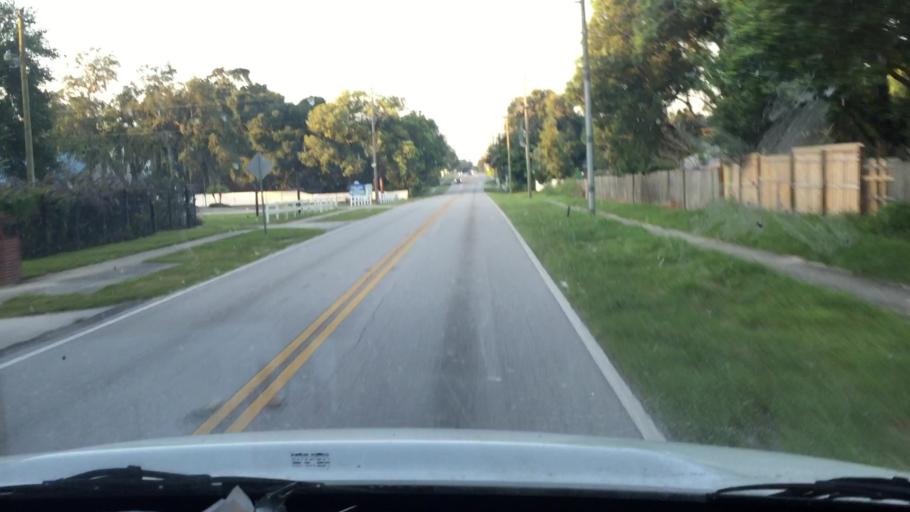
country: US
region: Florida
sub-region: Hillsborough County
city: Seffner
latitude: 27.9627
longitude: -82.2777
